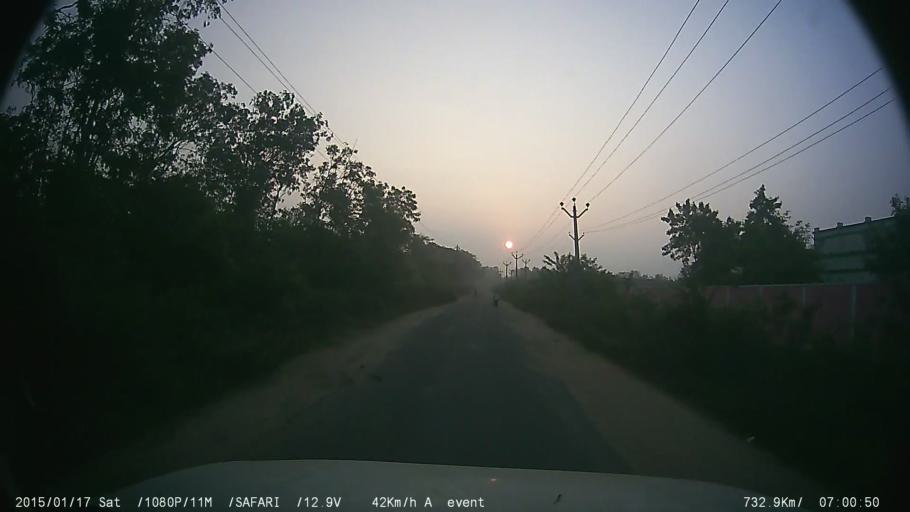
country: IN
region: Tamil Nadu
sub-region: Kancheepuram
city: Singapperumalkovil
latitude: 12.7961
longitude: 80.0157
